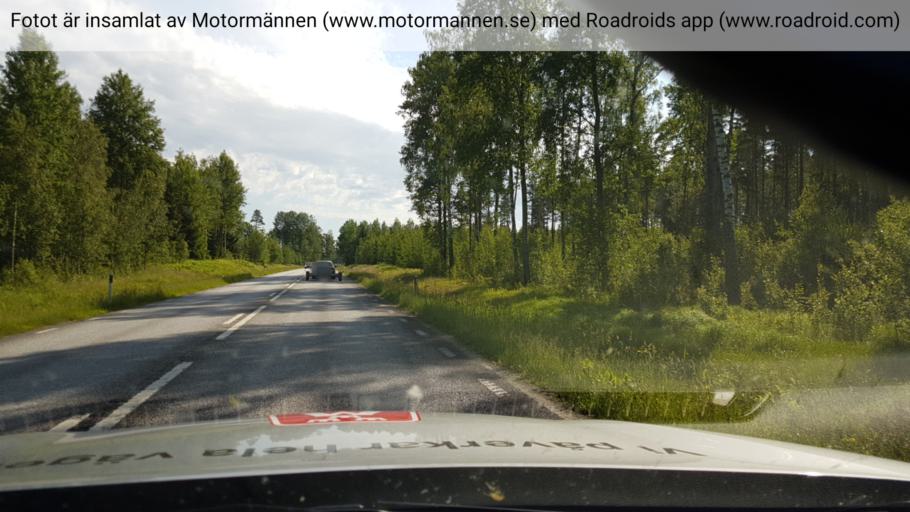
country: SE
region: OErebro
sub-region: Kumla Kommun
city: Hallabrottet
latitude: 59.1328
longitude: 15.2481
